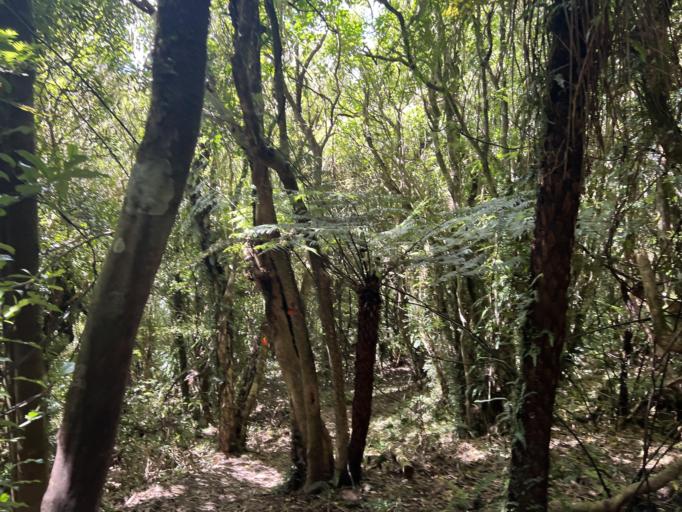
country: NZ
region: Wellington
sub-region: Kapiti Coast District
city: Paraparaumu
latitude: -40.8796
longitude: 175.0909
